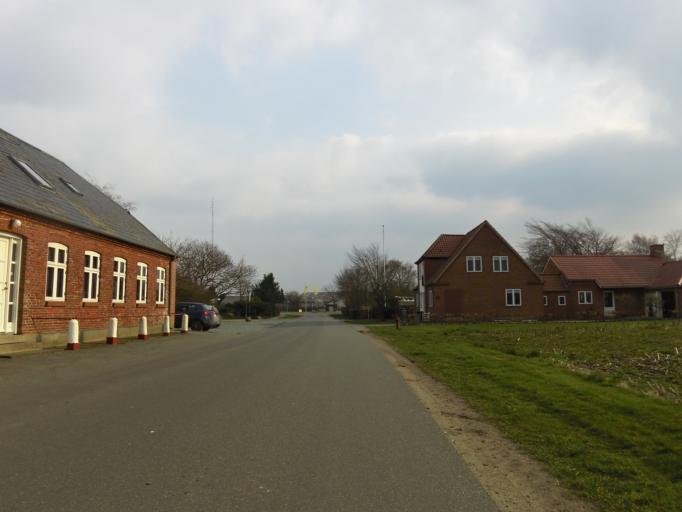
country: DK
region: South Denmark
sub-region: Esbjerg Kommune
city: Ribe
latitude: 55.3590
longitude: 8.7355
